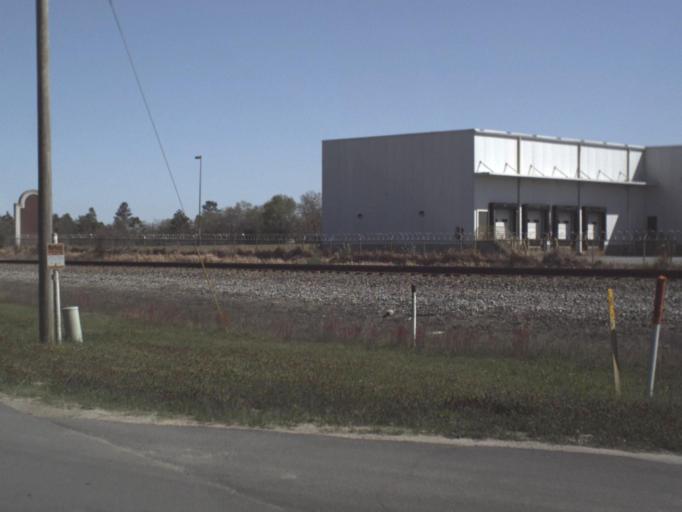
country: US
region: Florida
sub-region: Walton County
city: DeFuniak Springs
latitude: 30.7374
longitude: -86.1674
